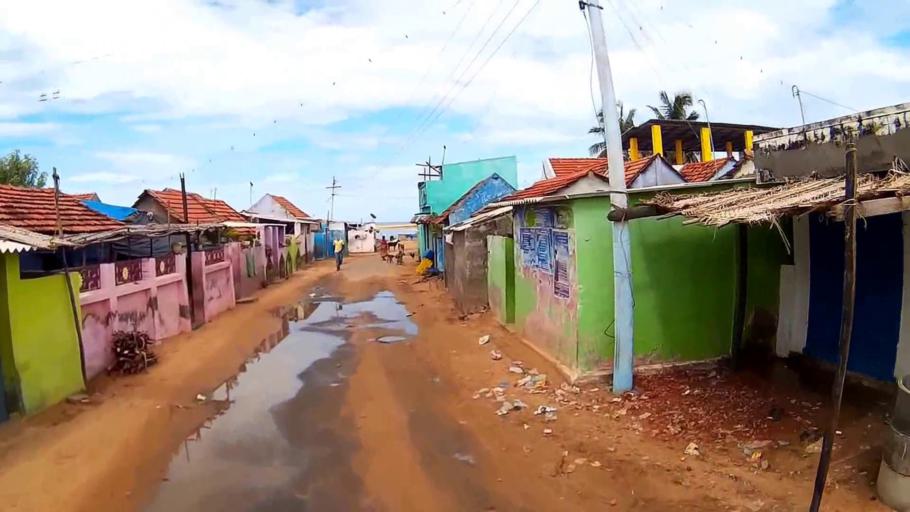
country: IN
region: Tamil Nadu
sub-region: Thoothukkudi
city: Udankudi
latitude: 8.3790
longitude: 78.0565
